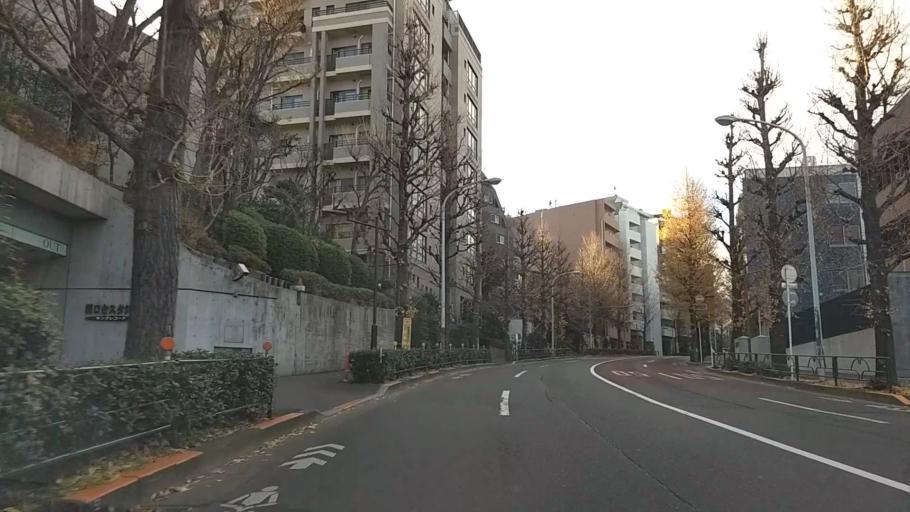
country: JP
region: Tokyo
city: Tokyo
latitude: 35.7120
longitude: 139.7288
